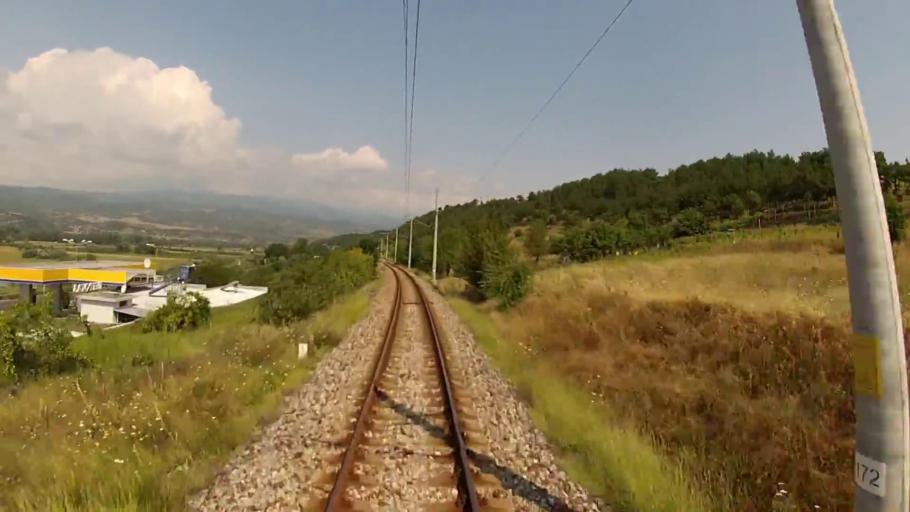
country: BG
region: Blagoevgrad
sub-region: Obshtina Strumyani
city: Strumyani
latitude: 41.6365
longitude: 23.2016
